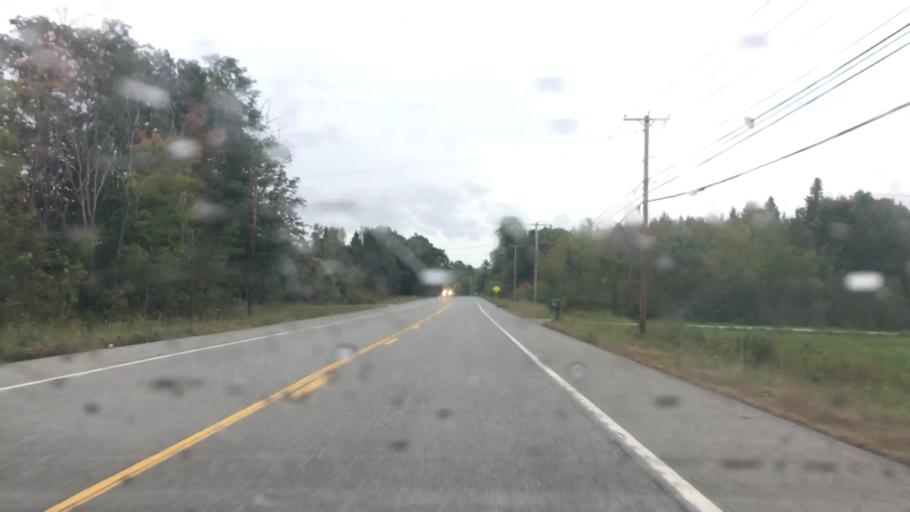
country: US
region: Maine
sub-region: Penobscot County
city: Orrington
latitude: 44.7138
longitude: -68.8269
